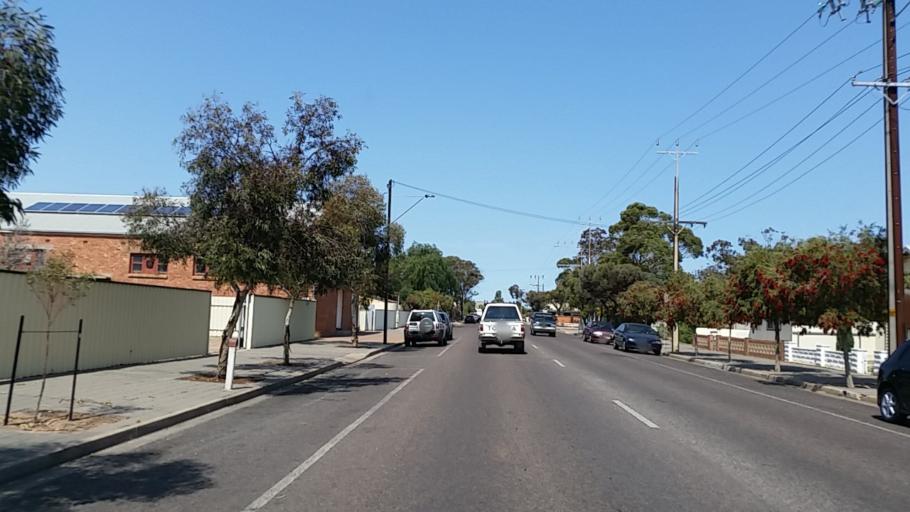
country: AU
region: South Australia
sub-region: Port Augusta
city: Port Augusta West
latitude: -32.4926
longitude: 137.7610
